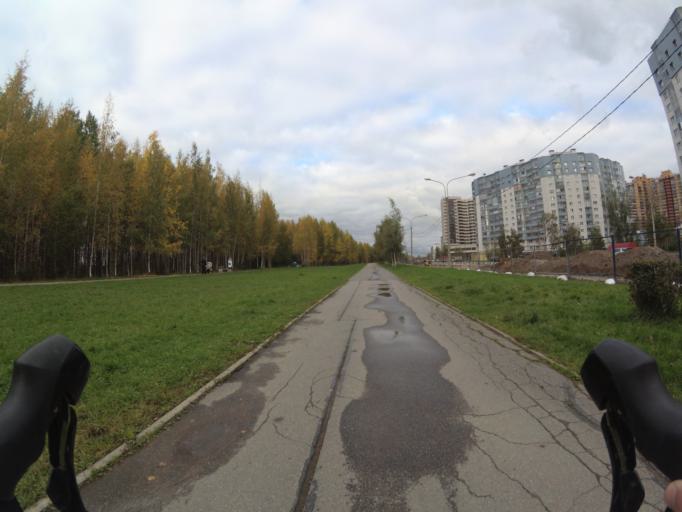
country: RU
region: Leningrad
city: Untolovo
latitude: 59.9976
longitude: 30.1926
